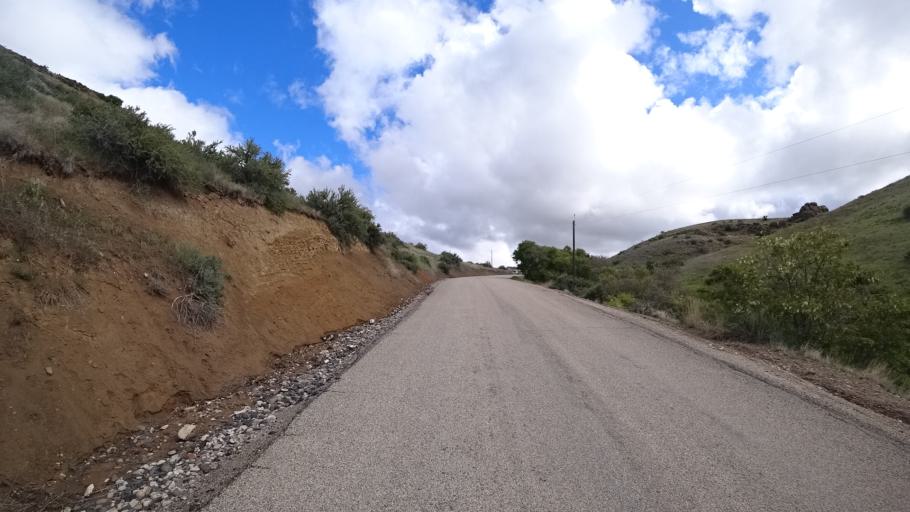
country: US
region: Idaho
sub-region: Ada County
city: Garden City
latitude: 43.7335
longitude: -116.2297
